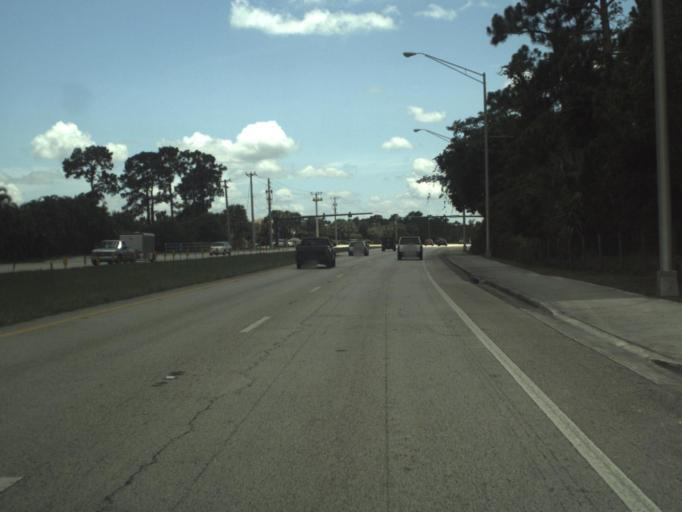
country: US
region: Florida
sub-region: Martin County
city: Palm City
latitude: 27.1482
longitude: -80.2448
